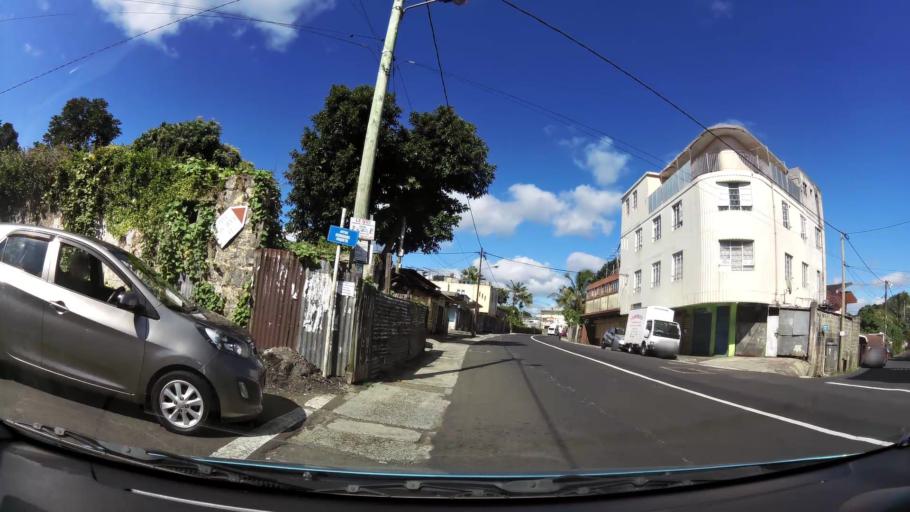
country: MU
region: Plaines Wilhems
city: Vacoas
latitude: -20.3044
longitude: 57.4924
